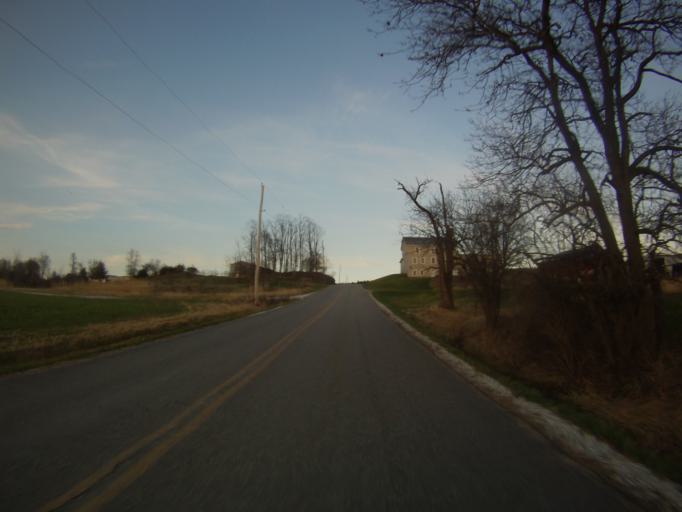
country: US
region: Vermont
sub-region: Addison County
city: Middlebury (village)
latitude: 44.0206
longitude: -73.2330
